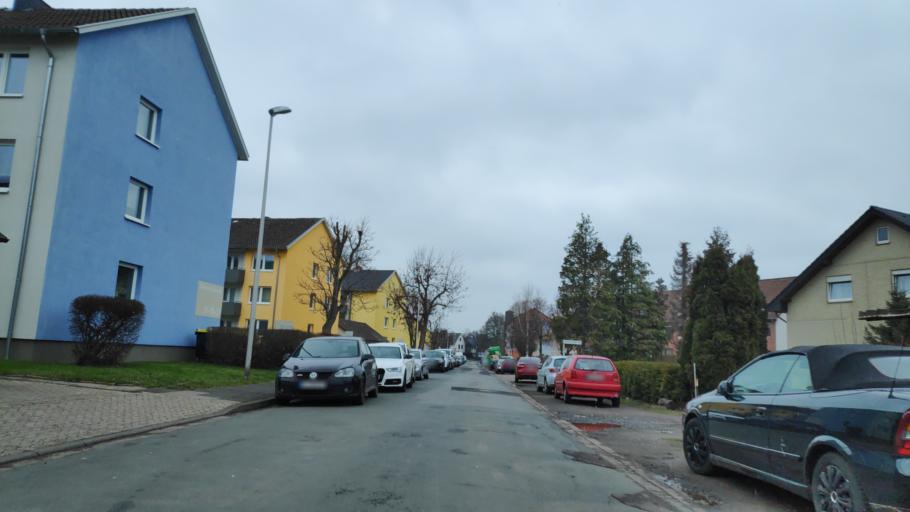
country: DE
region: North Rhine-Westphalia
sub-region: Regierungsbezirk Detmold
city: Minden
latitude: 52.3052
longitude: 8.8967
